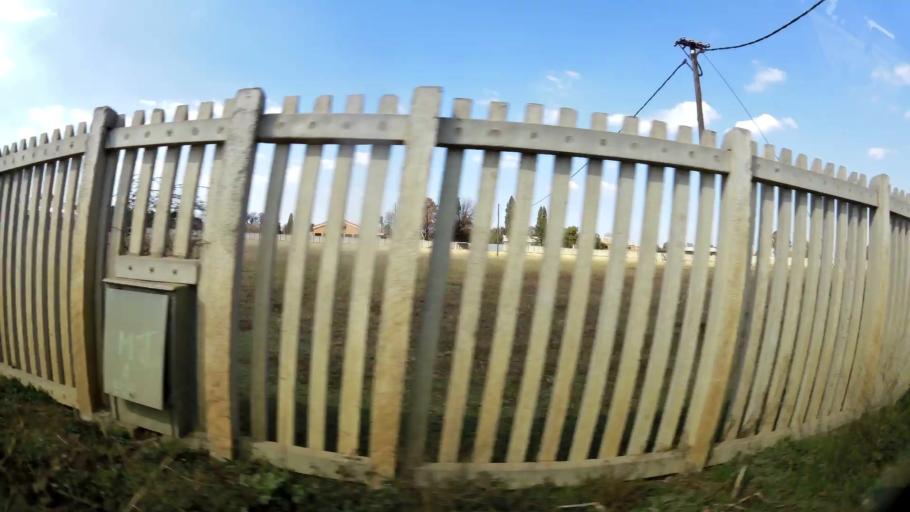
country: ZA
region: Gauteng
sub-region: Ekurhuleni Metropolitan Municipality
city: Benoni
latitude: -26.1071
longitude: 28.3640
